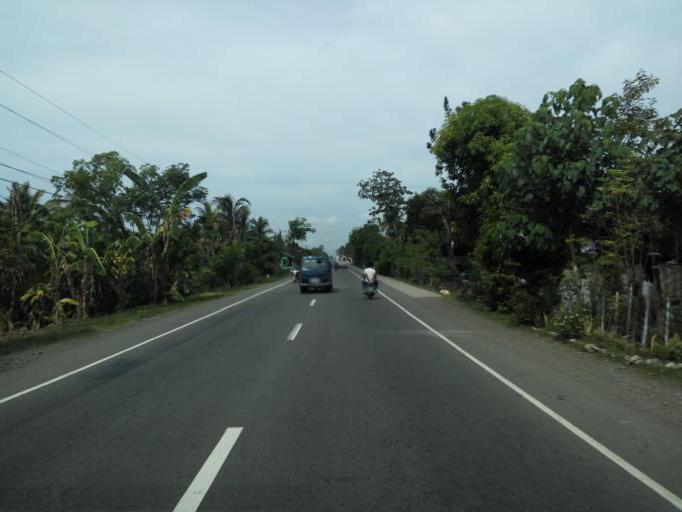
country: PH
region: Cagayan Valley
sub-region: Province of Isabela
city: Naguilian
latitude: 17.0058
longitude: 121.8286
